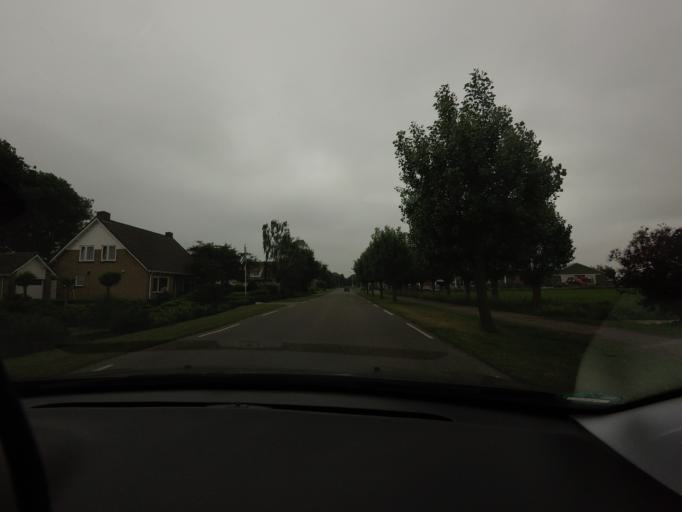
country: NL
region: South Holland
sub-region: Gemeente Vlist
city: Haastrecht
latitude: 52.0531
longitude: 4.8114
